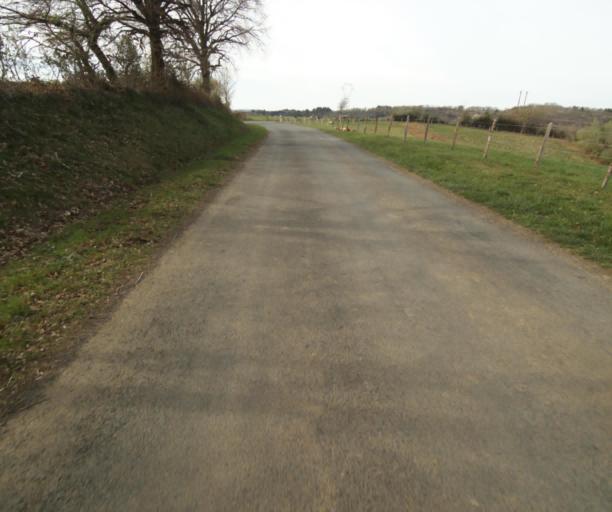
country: FR
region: Limousin
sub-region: Departement de la Correze
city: Chamboulive
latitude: 45.4203
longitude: 1.7830
